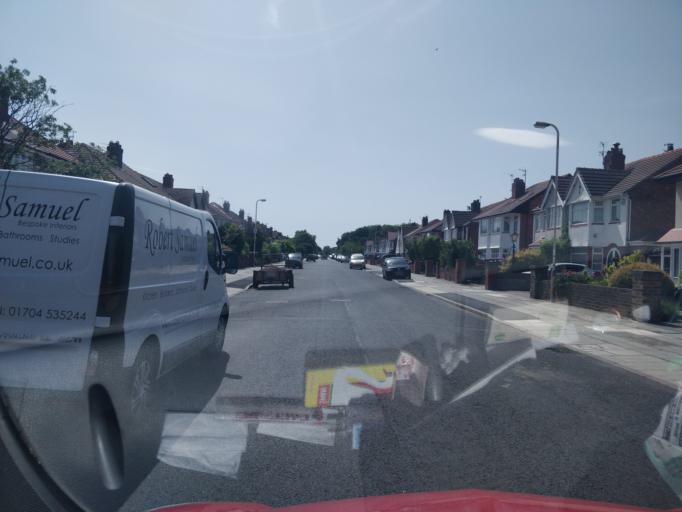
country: GB
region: England
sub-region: Lancashire
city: Banks
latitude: 53.6655
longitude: -2.9561
